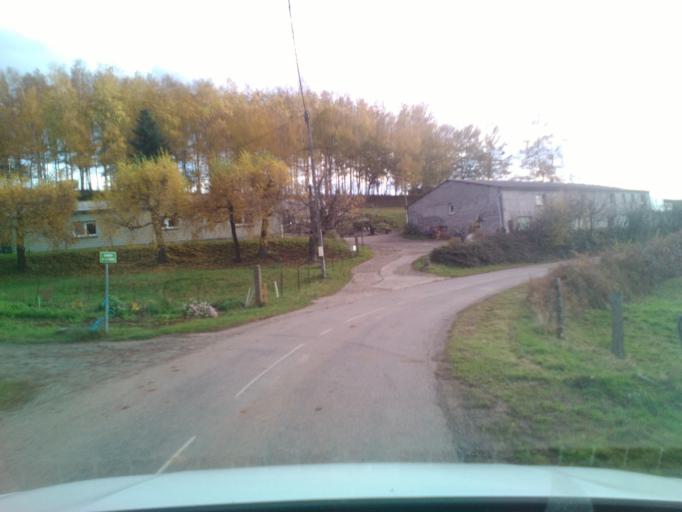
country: FR
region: Lorraine
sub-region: Departement des Vosges
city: Senones
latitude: 48.3749
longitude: 7.0014
